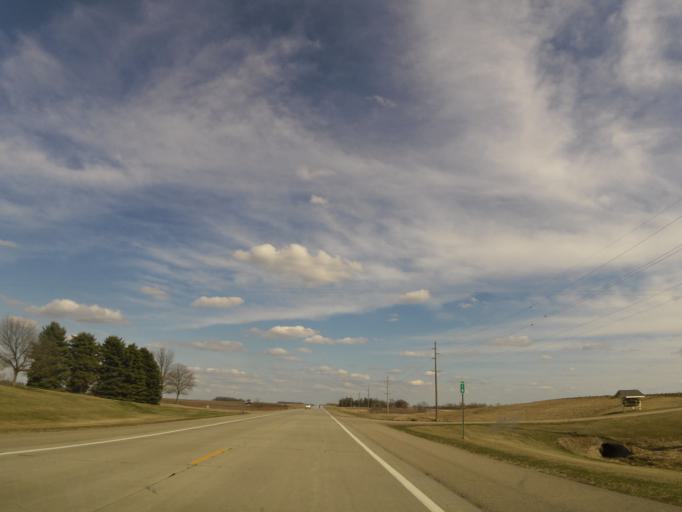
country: US
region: Minnesota
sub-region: Lac qui Parle County
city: Madison
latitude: 44.9358
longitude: -96.1468
